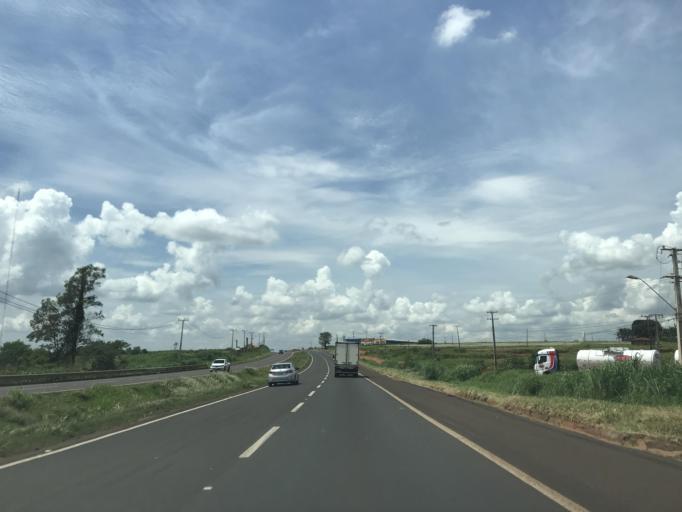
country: BR
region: Parana
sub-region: Alto Parana
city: Alto Parana
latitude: -23.2089
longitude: -52.1929
